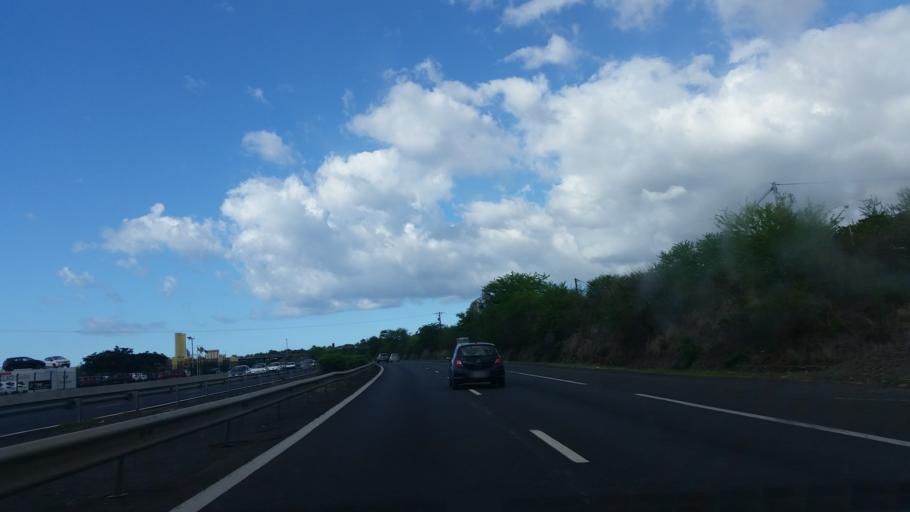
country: RE
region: Reunion
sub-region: Reunion
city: Le Port
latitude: -20.9755
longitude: 55.2976
